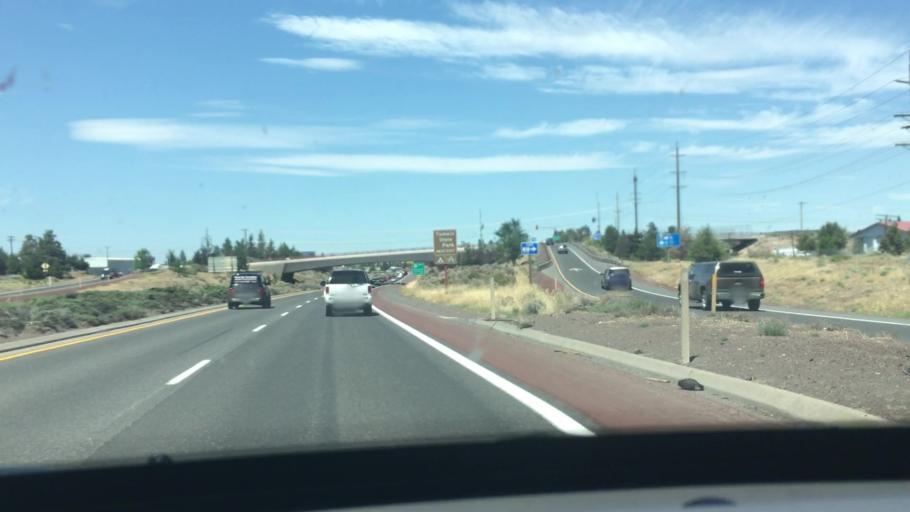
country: US
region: Oregon
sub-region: Deschutes County
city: Bend
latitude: 44.0886
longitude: -121.3009
